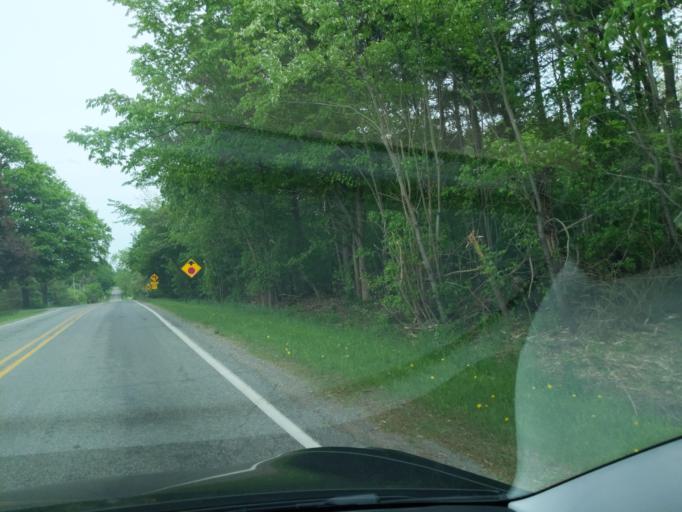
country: US
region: Michigan
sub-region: Ingham County
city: Mason
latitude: 42.5332
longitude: -84.4272
